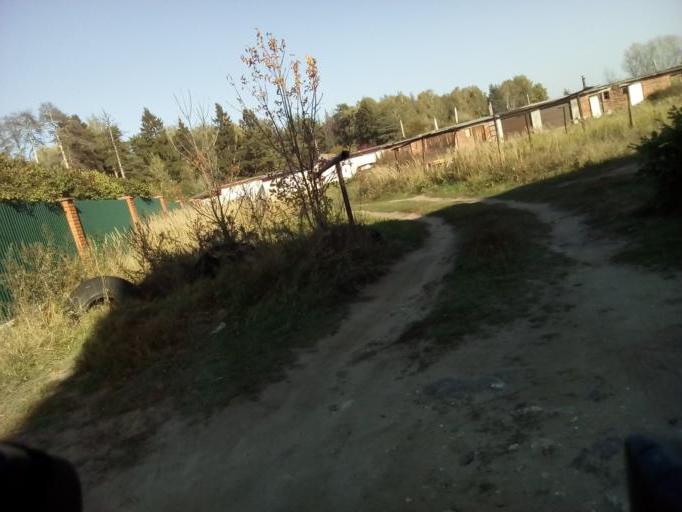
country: RU
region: Moskovskaya
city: Malyshevo
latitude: 55.5586
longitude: 38.3213
